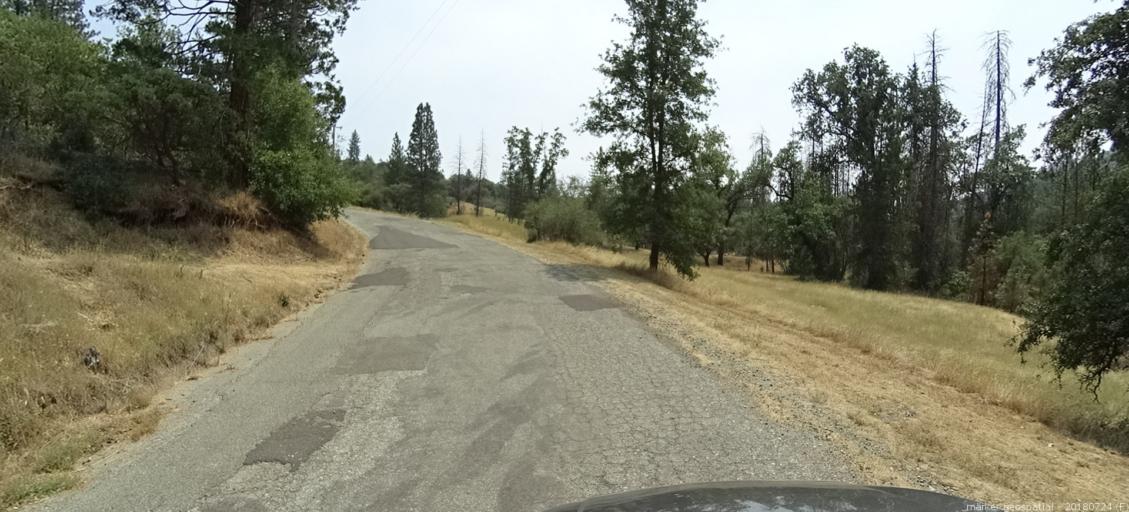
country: US
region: California
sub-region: Madera County
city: Oakhurst
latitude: 37.2478
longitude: -119.5590
